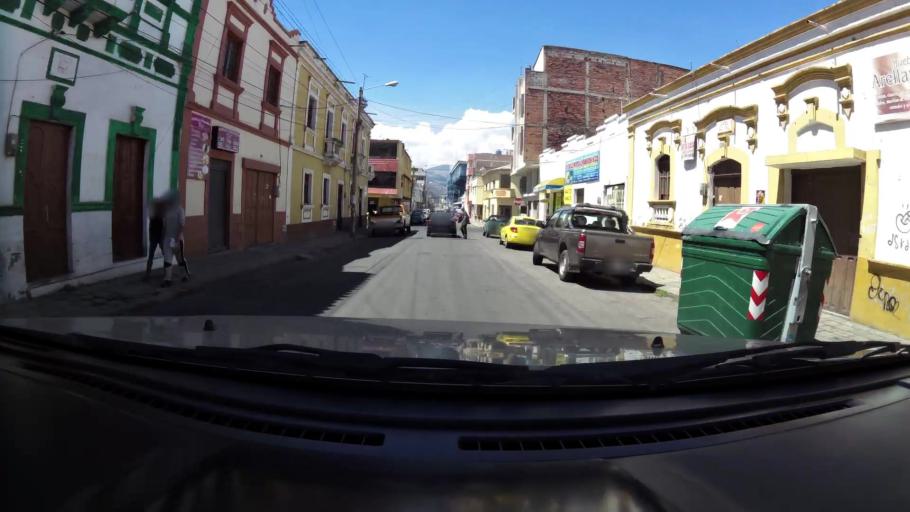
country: EC
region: Chimborazo
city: Riobamba
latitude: -1.6683
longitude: -78.6500
